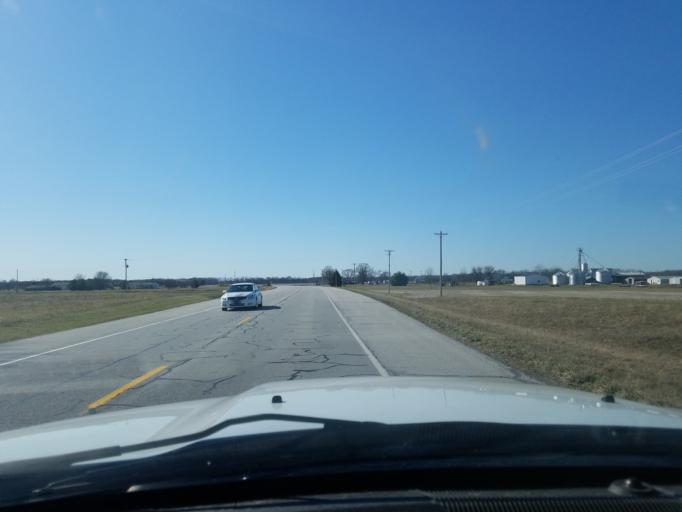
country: US
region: Indiana
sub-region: Shelby County
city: Shelbyville
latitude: 39.5038
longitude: -85.8369
